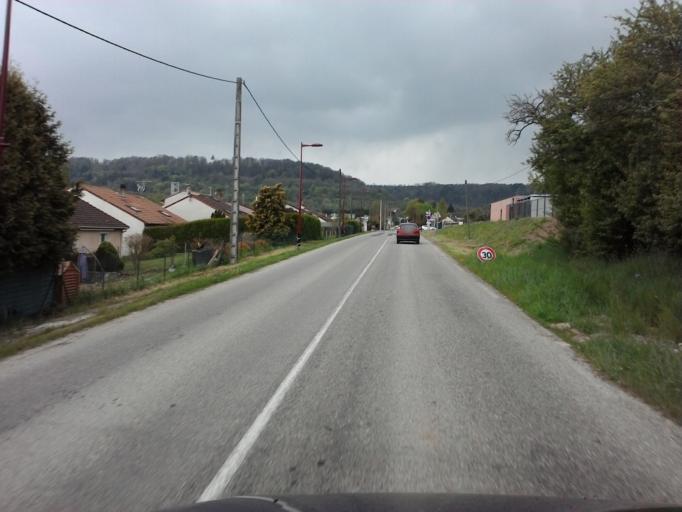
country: FR
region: Lorraine
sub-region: Departement de Meurthe-et-Moselle
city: Blenod-les-Toul
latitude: 48.6009
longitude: 5.8452
